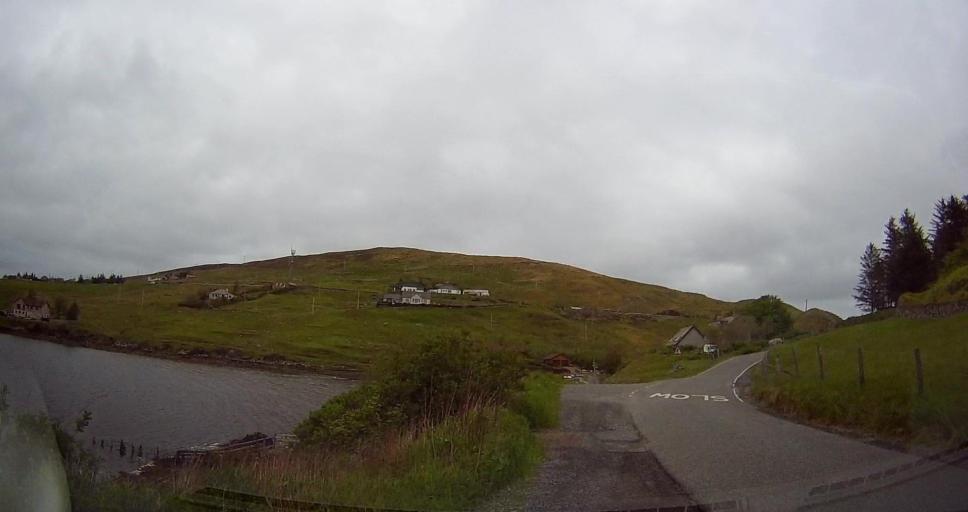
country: GB
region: Scotland
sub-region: Shetland Islands
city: Lerwick
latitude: 60.3507
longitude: -1.2647
